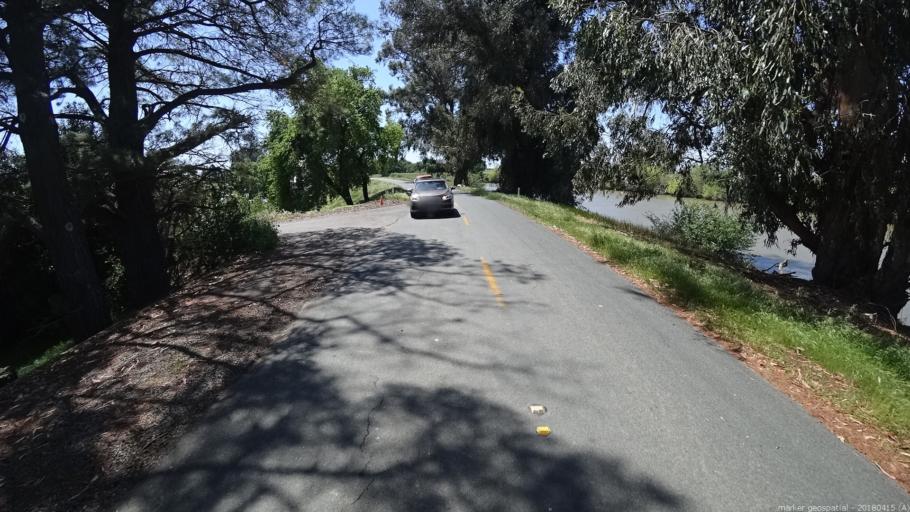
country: US
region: California
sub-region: Sacramento County
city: Walnut Grove
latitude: 38.2840
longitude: -121.5874
